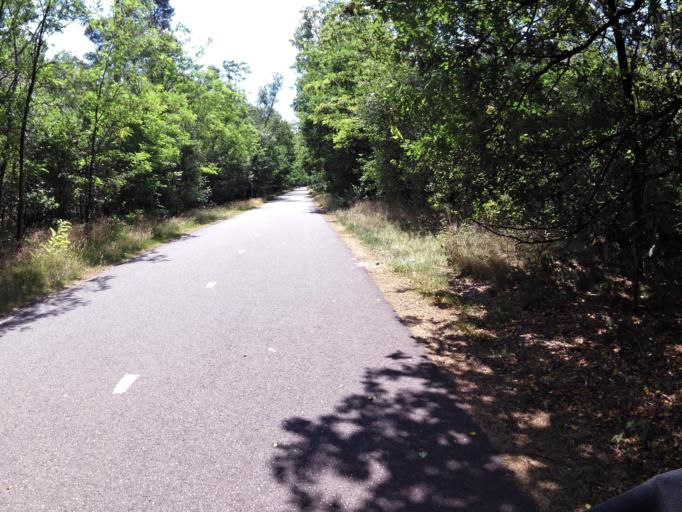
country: NL
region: North Brabant
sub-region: Gemeente Oisterwijk
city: Oisterwijk
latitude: 51.5595
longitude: 5.1987
